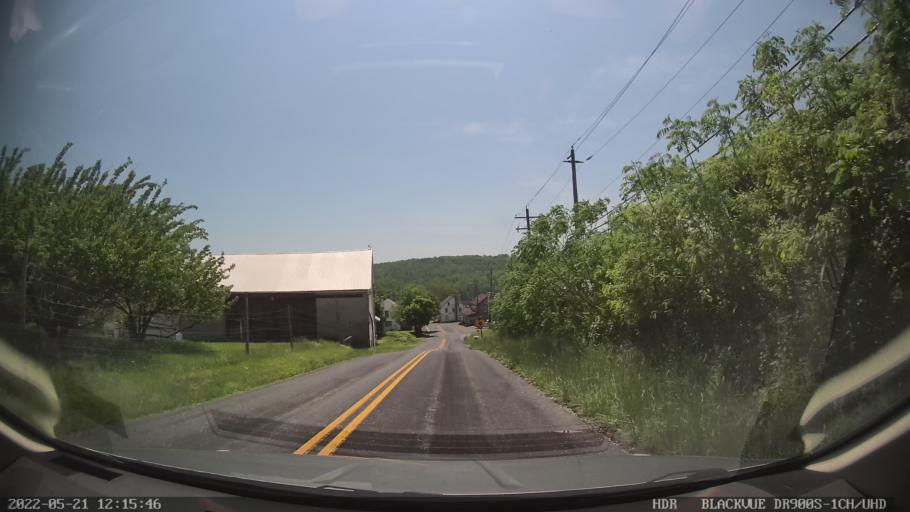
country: US
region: Pennsylvania
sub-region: Berks County
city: Red Lion
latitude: 40.4277
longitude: -75.6617
